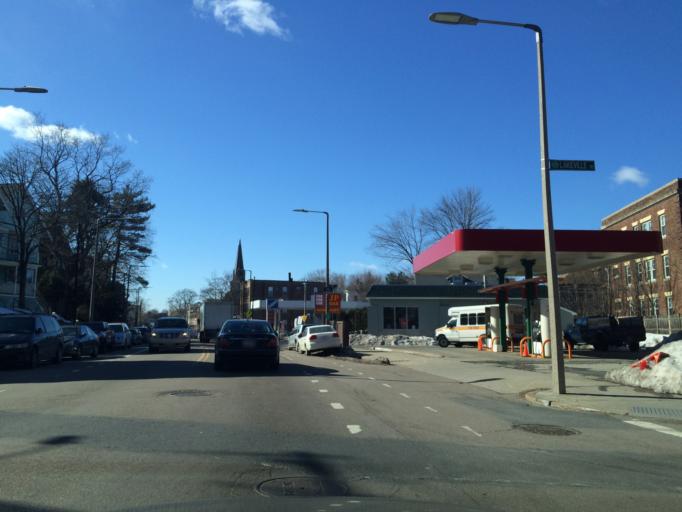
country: US
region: Massachusetts
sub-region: Suffolk County
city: Jamaica Plain
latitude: 42.3161
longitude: -71.1140
